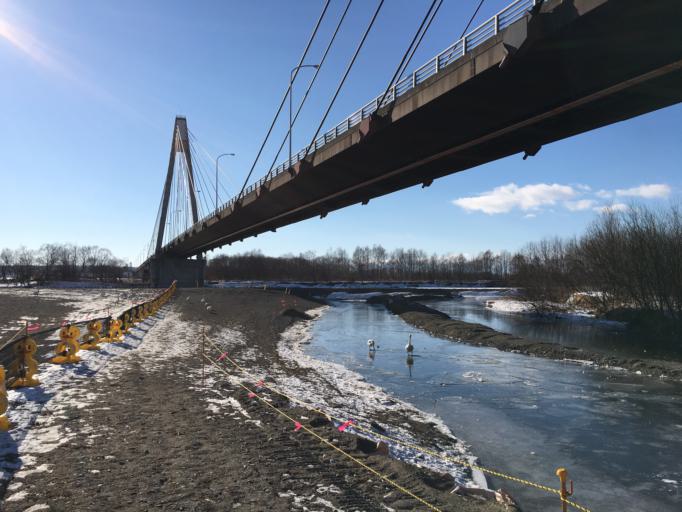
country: JP
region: Hokkaido
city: Obihiro
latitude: 42.9317
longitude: 143.2934
